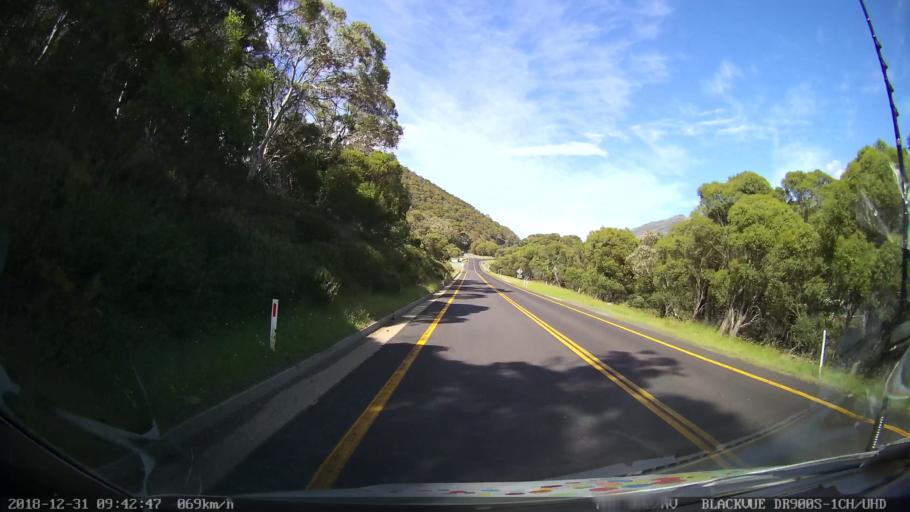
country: AU
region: New South Wales
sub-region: Snowy River
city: Jindabyne
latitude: -36.4984
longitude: 148.3192
